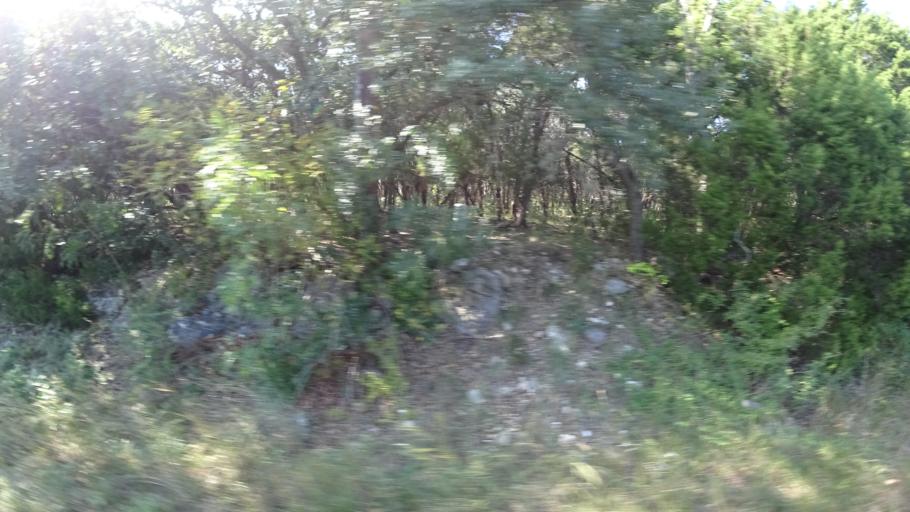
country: US
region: Texas
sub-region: Travis County
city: West Lake Hills
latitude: 30.2895
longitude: -97.8023
